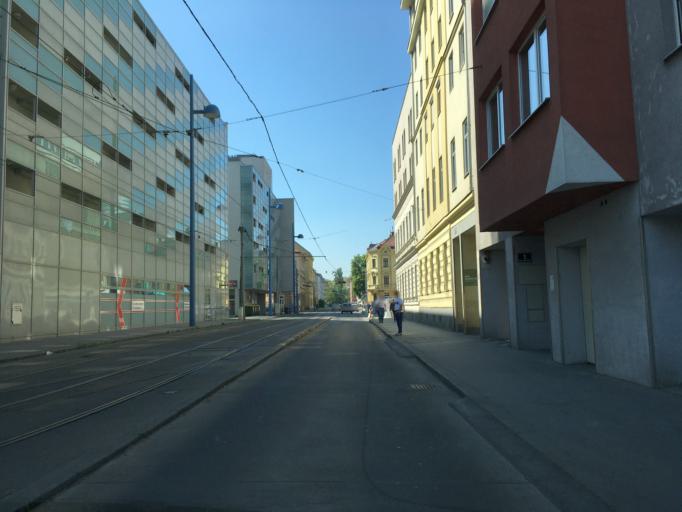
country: AT
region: Vienna
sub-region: Wien Stadt
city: Vienna
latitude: 48.2562
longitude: 16.3984
